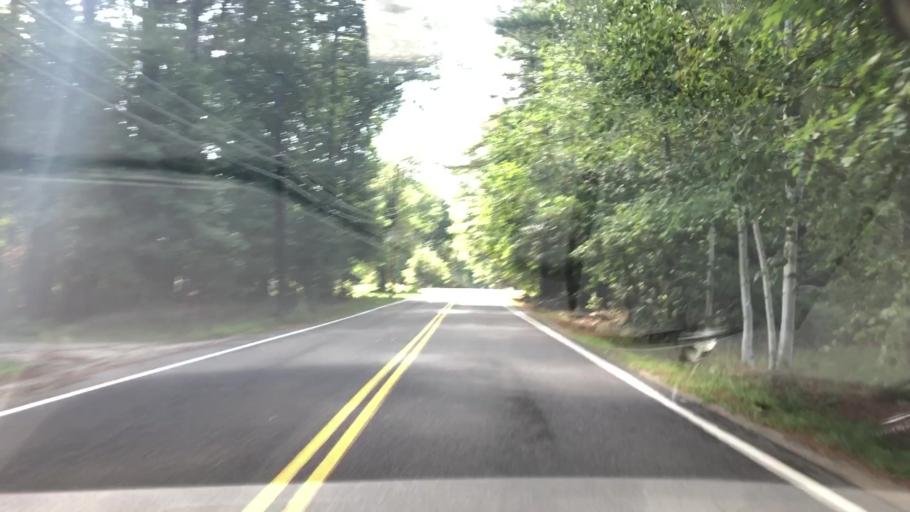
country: US
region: New Hampshire
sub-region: Hillsborough County
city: Milford
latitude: 42.8366
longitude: -71.5967
